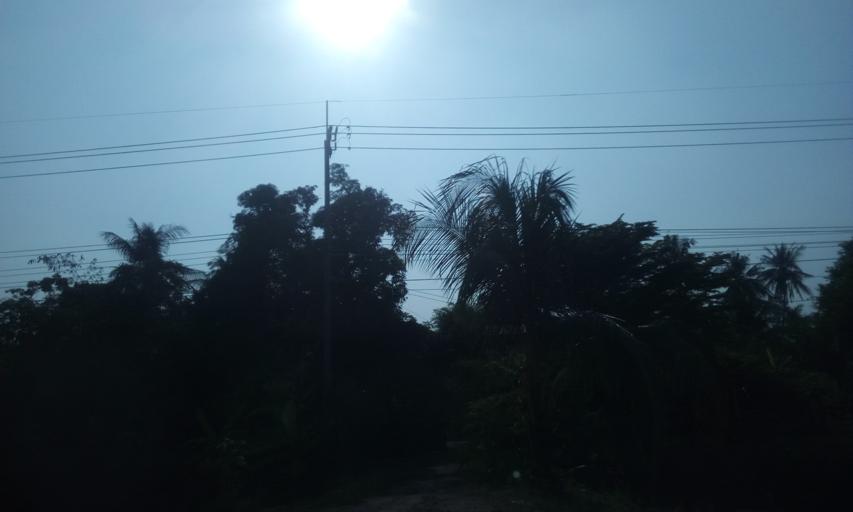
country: TH
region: Sing Buri
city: Phrom Buri
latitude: 14.7718
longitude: 100.4376
